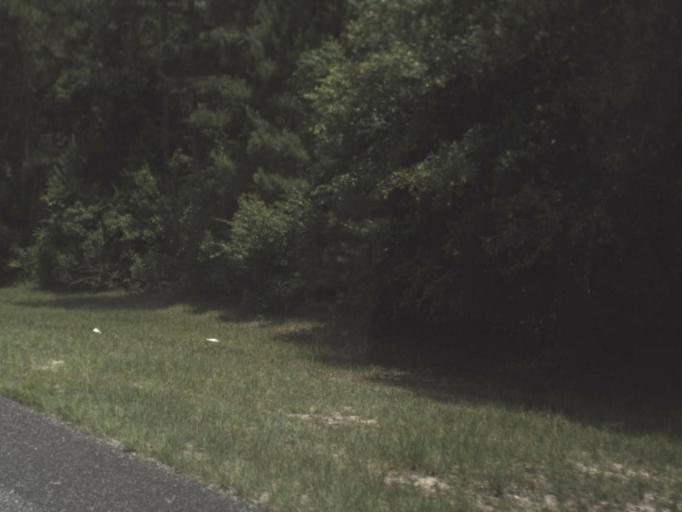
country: US
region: Florida
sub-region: Alachua County
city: Newberry
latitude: 29.6539
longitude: -82.5338
